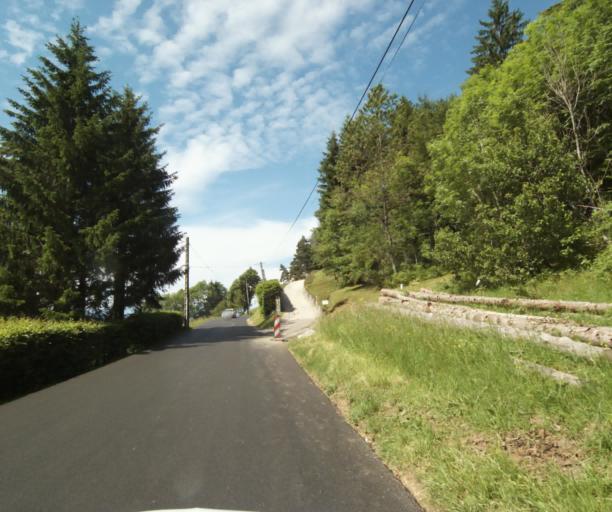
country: FR
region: Rhone-Alpes
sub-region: Departement de la Haute-Savoie
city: Perrignier
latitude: 46.2904
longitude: 6.4758
